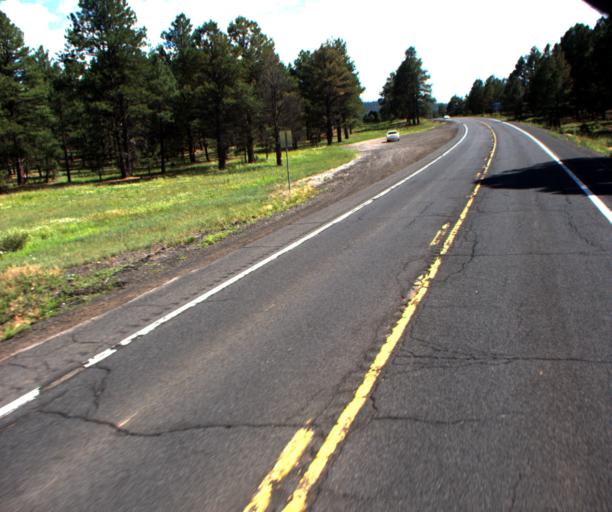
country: US
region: Arizona
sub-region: Coconino County
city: Williams
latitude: 35.2667
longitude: -112.1500
